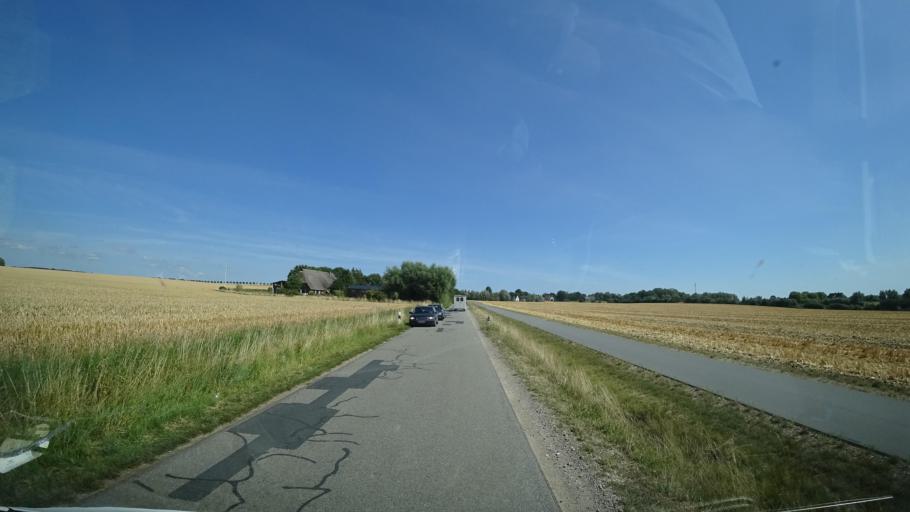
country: DE
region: Mecklenburg-Vorpommern
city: Blowatz
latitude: 54.0223
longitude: 11.5540
